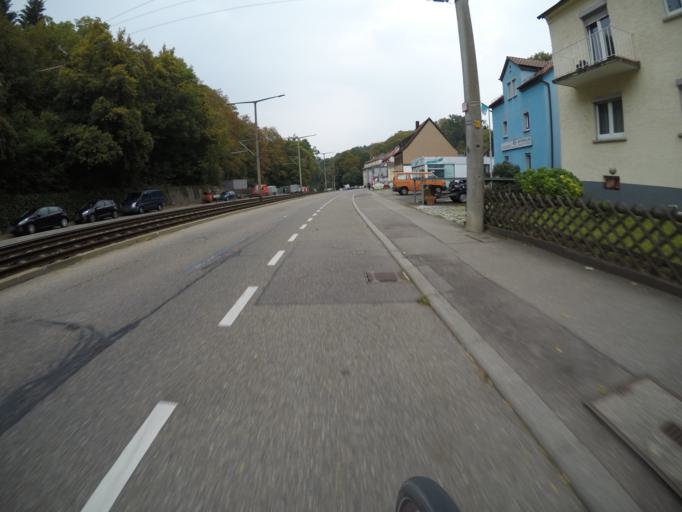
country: DE
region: Baden-Wuerttemberg
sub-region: Regierungsbezirk Stuttgart
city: Leinfelden-Echterdingen
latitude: 48.7422
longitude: 9.1318
